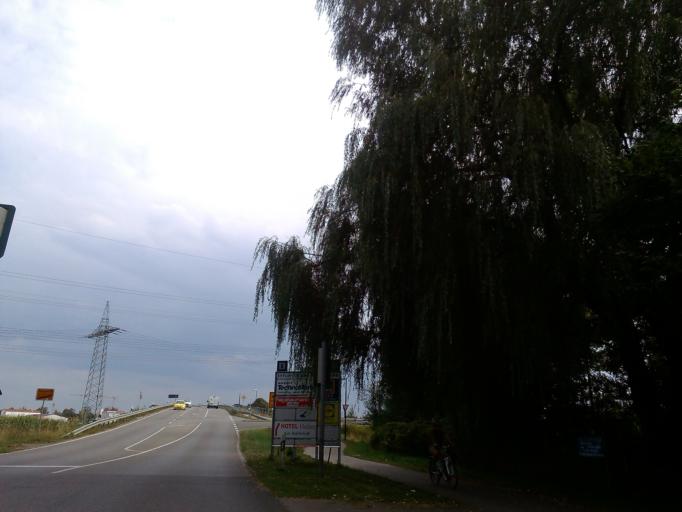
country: DE
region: Bavaria
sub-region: Upper Bavaria
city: Puchheim
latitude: 48.1454
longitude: 11.3510
